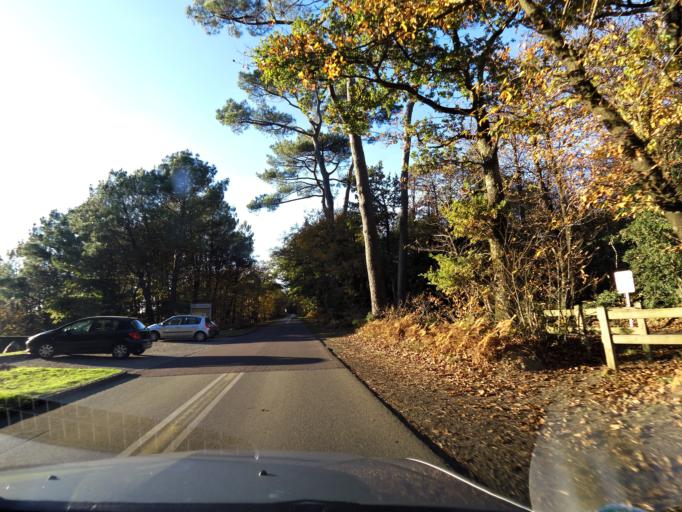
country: FR
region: Brittany
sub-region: Departement d'Ille-et-Vilaine
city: Pance
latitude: 47.8838
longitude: -1.6666
